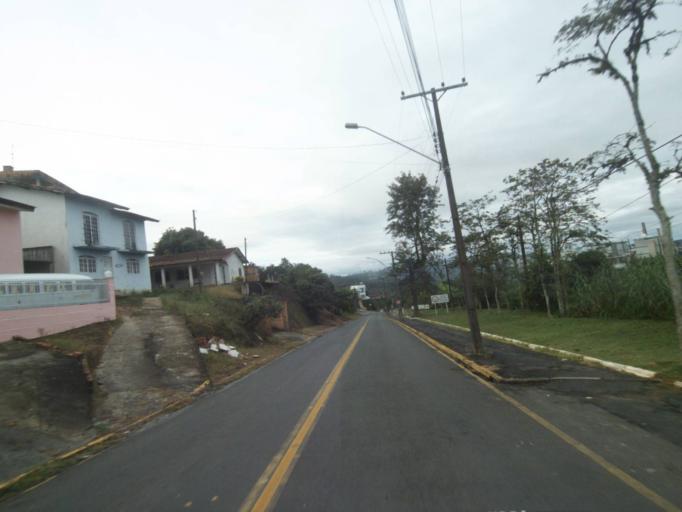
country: BR
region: Parana
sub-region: Telemaco Borba
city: Telemaco Borba
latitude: -24.3184
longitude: -50.6173
